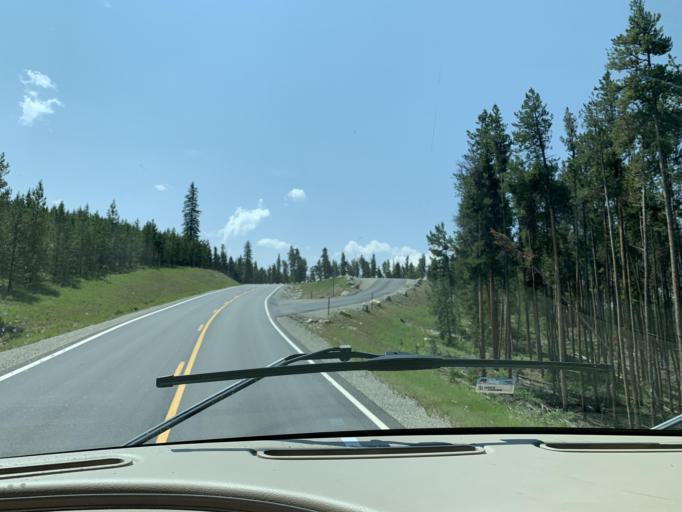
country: US
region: Colorado
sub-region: Chaffee County
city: Buena Vista
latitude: 38.8473
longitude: -106.4891
